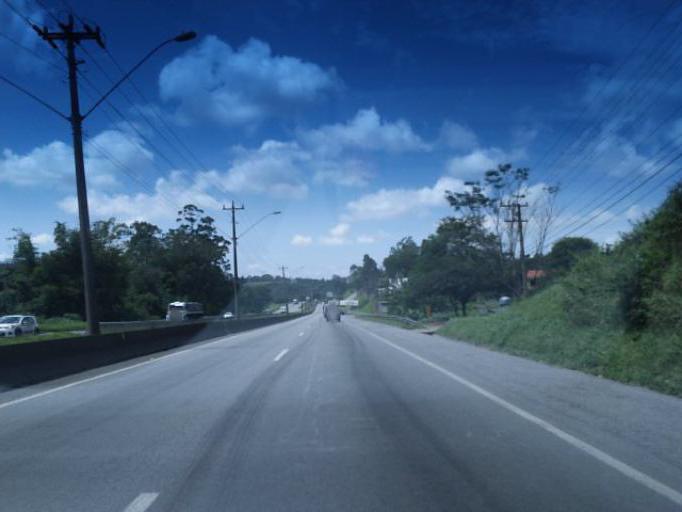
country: BR
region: Sao Paulo
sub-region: Itapecerica Da Serra
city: Itapecerica da Serra
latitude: -23.7529
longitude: -46.9017
